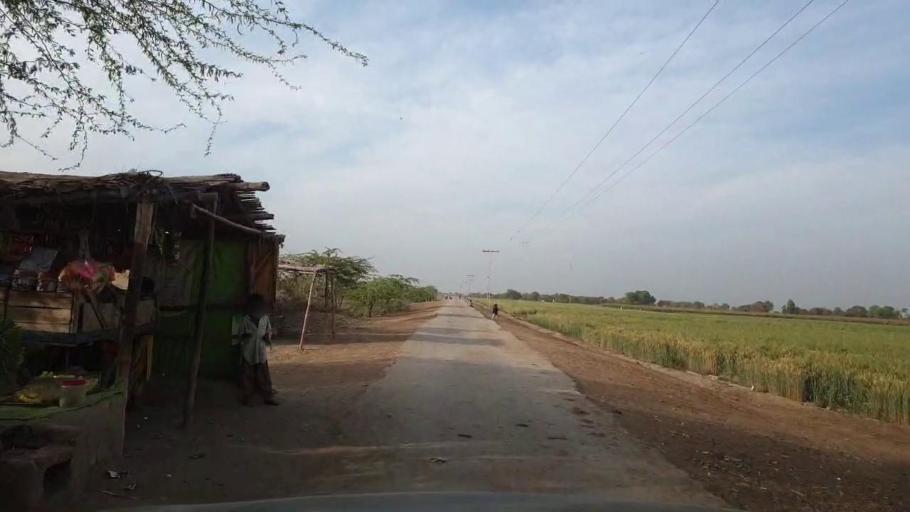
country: PK
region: Sindh
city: Kunri
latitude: 25.1968
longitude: 69.5199
